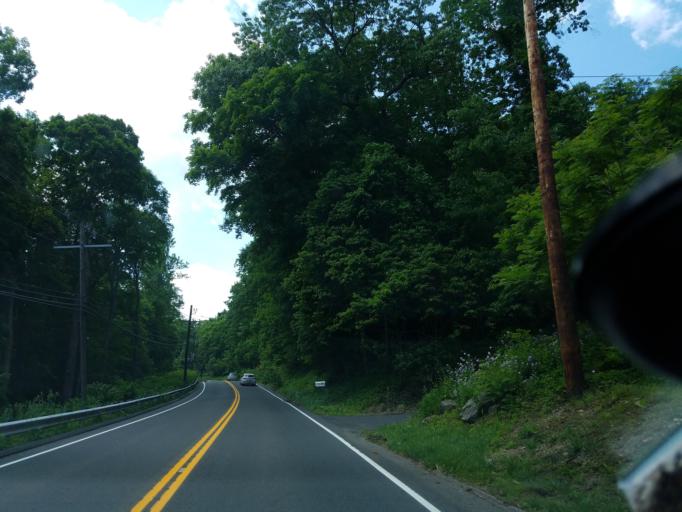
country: US
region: New York
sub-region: Putnam County
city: Putnam Lake
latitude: 41.4791
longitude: -73.4664
